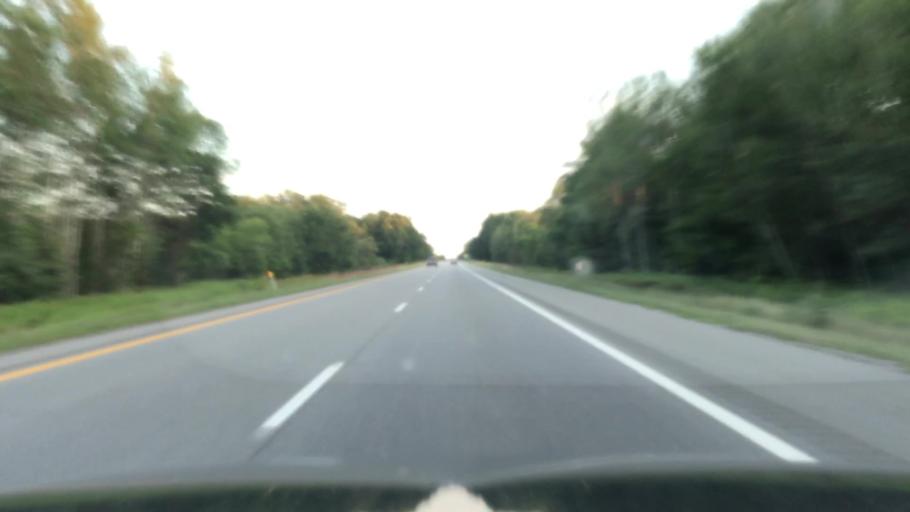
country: US
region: Michigan
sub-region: Montcalm County
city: Howard City
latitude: 43.5185
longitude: -85.4868
